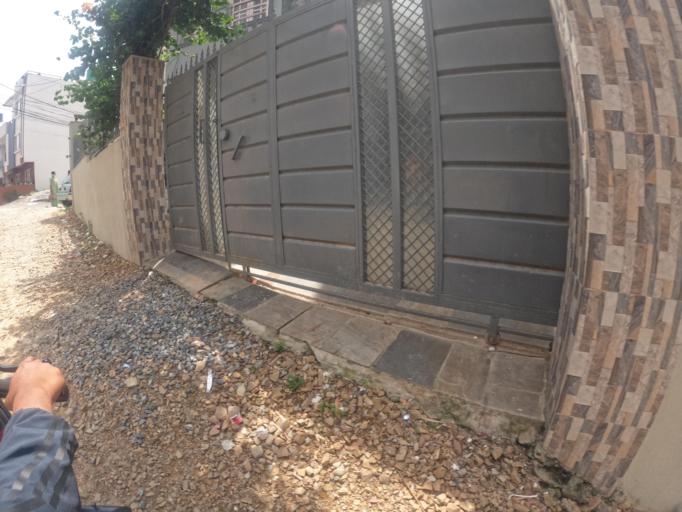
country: NP
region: Central Region
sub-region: Bagmati Zone
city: Kathmandu
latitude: 27.6801
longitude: 85.3690
